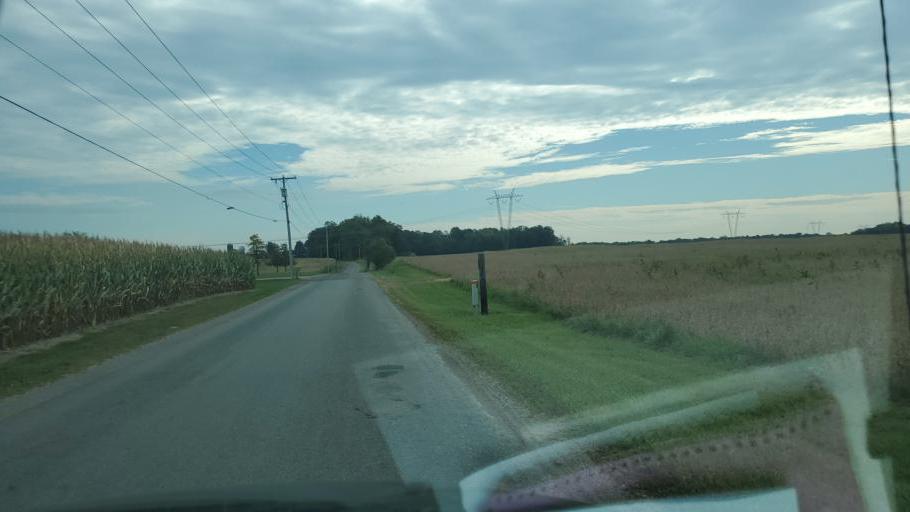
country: US
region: Ohio
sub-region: Richland County
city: Lexington
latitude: 40.5861
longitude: -82.6594
